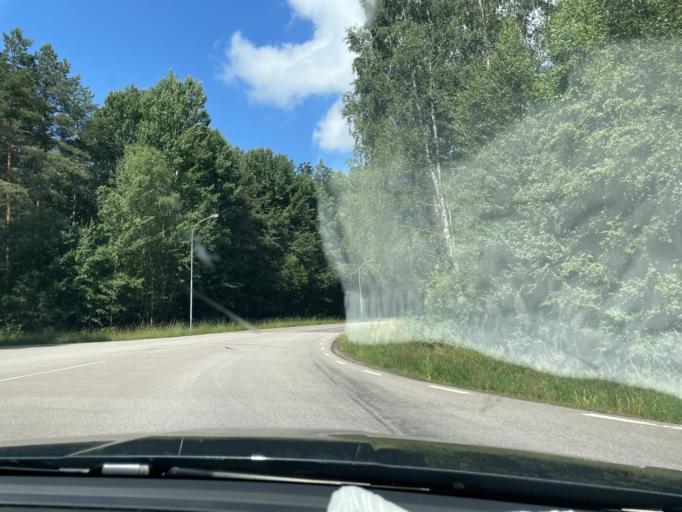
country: SE
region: Kronoberg
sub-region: Vaxjo Kommun
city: Vaexjoe
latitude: 56.8491
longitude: 14.8584
